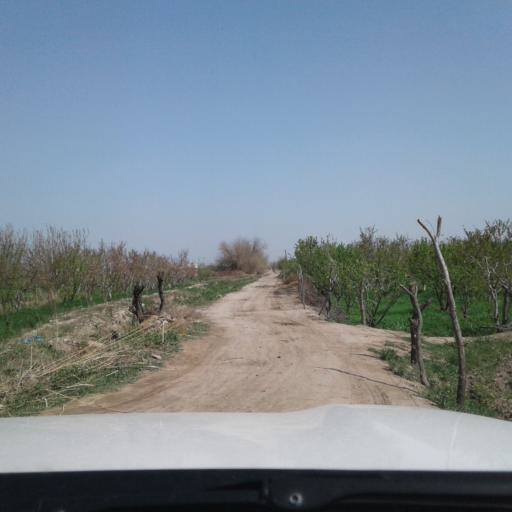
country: TM
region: Lebap
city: Turkmenabat
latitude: 38.9565
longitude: 63.6443
